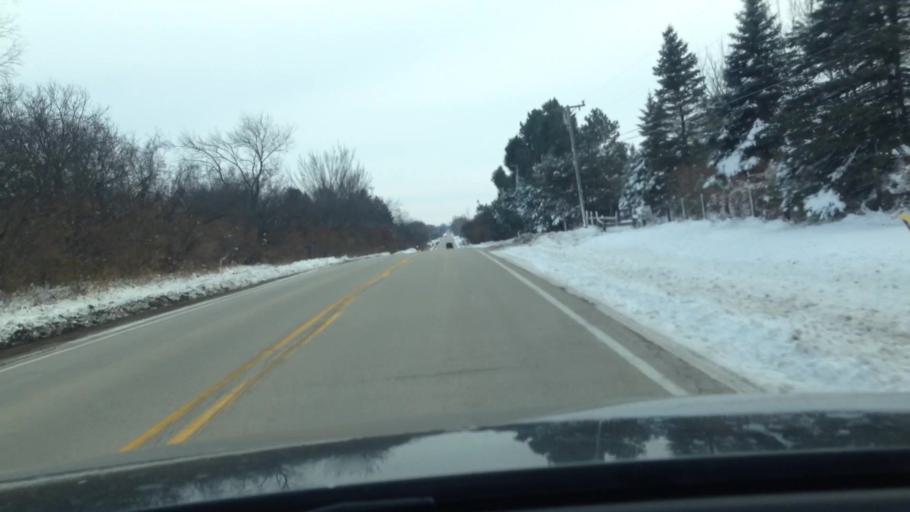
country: US
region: Illinois
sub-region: McHenry County
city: Woodstock
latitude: 42.3836
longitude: -88.4432
